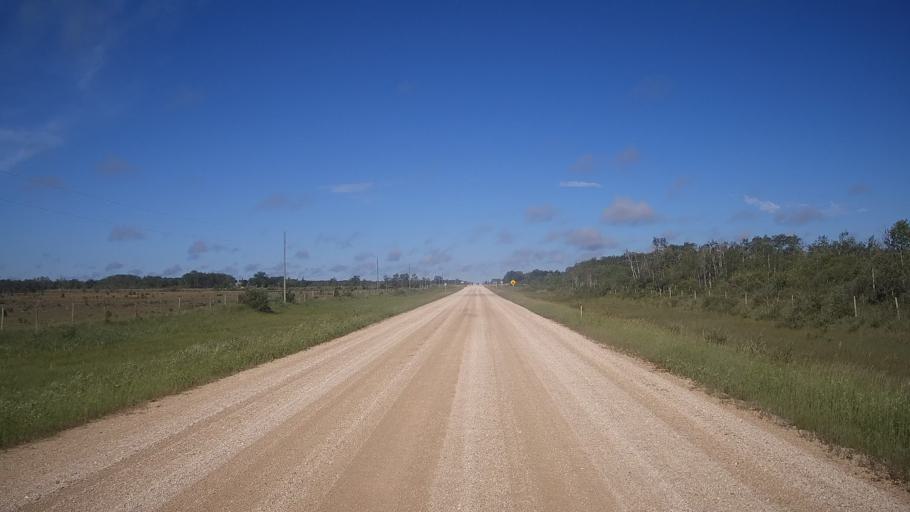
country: CA
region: Manitoba
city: Stonewall
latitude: 50.2411
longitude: -97.7285
